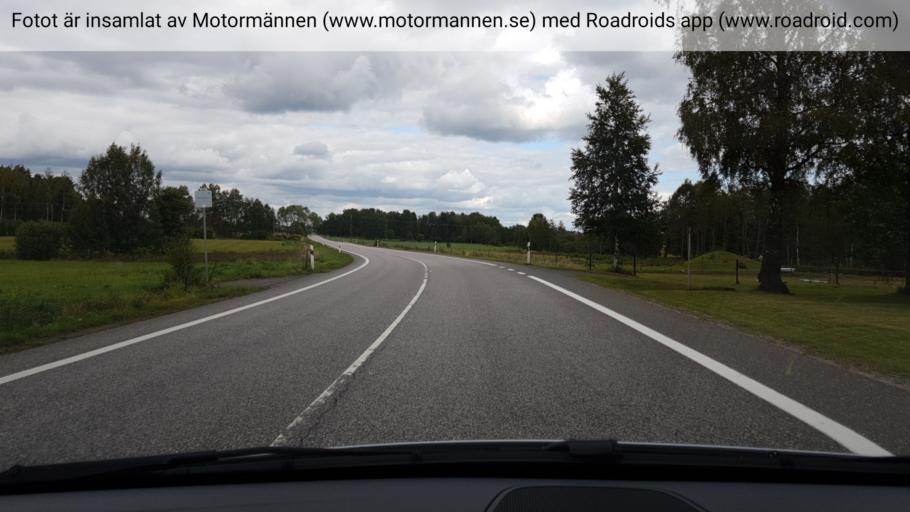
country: SE
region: Vaestra Goetaland
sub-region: Tidaholms Kommun
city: Tidaholm
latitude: 58.1495
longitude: 13.9189
